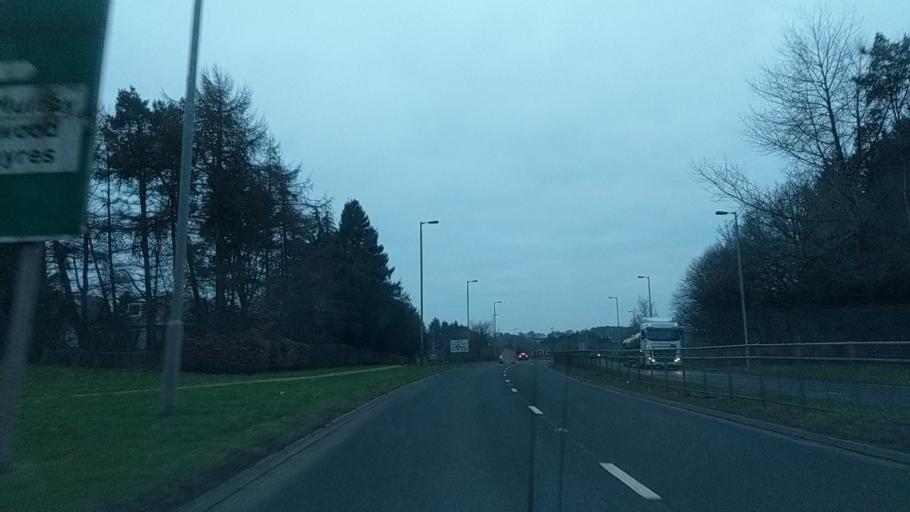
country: GB
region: Scotland
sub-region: South Lanarkshire
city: East Kilbride
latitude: 55.7595
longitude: -4.1648
